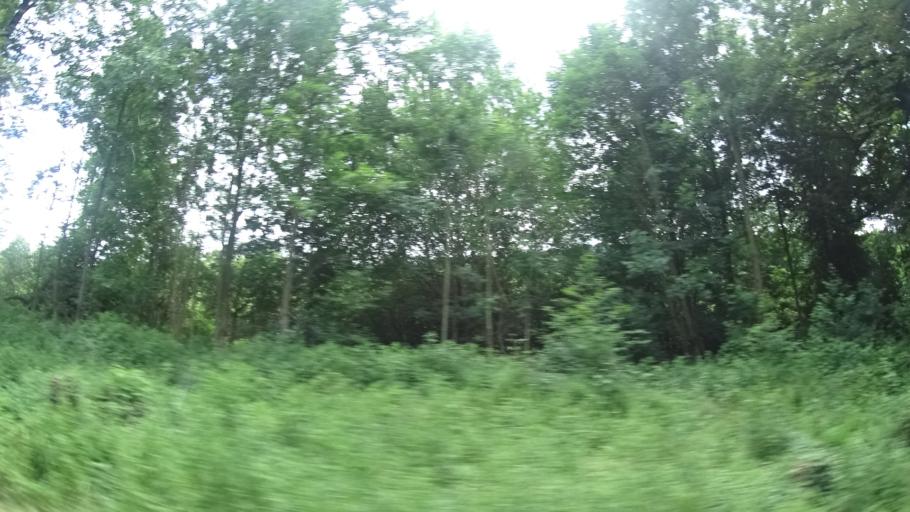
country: DE
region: Lower Saxony
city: Springe
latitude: 52.1890
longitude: 9.5777
